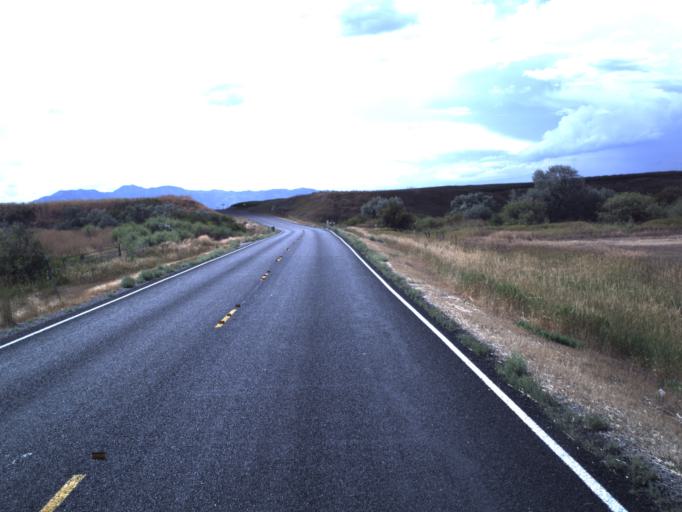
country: US
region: Utah
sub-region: Cache County
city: Richmond
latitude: 41.9247
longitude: -111.8495
